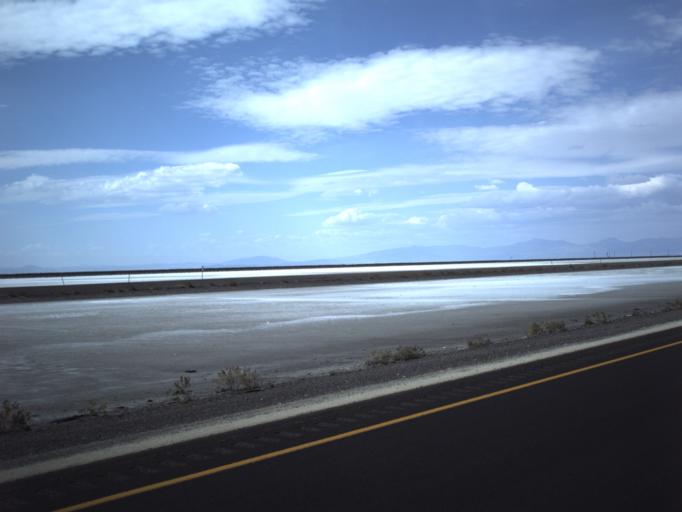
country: US
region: Utah
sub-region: Tooele County
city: Wendover
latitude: 40.7342
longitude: -113.6064
